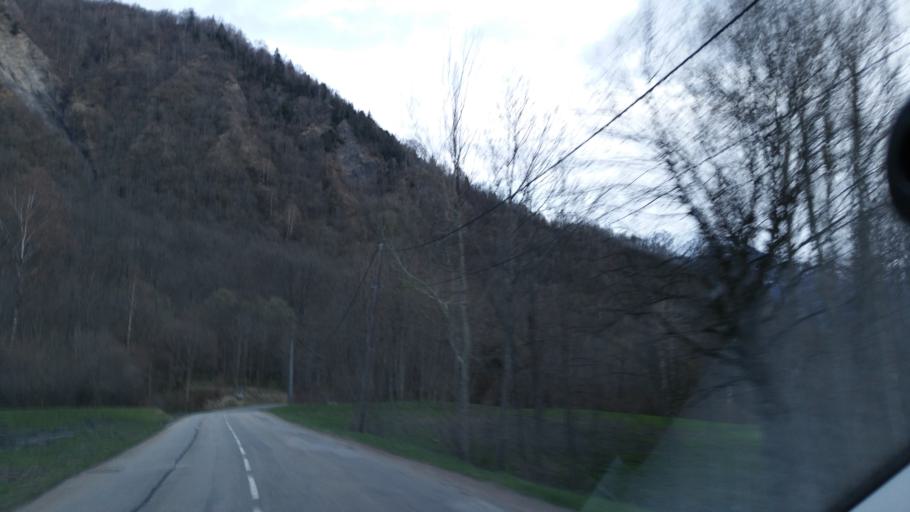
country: FR
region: Rhone-Alpes
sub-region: Departement de la Savoie
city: La Chambre
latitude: 45.3829
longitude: 6.3292
